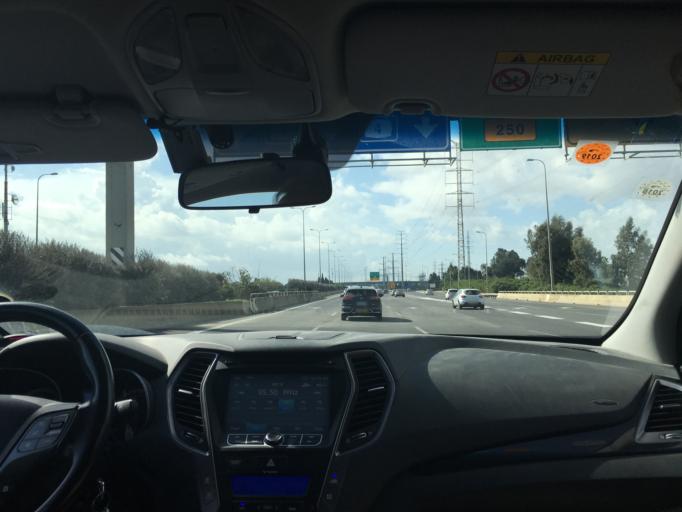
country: IL
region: Tel Aviv
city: Azor
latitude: 32.0276
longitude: 34.8277
